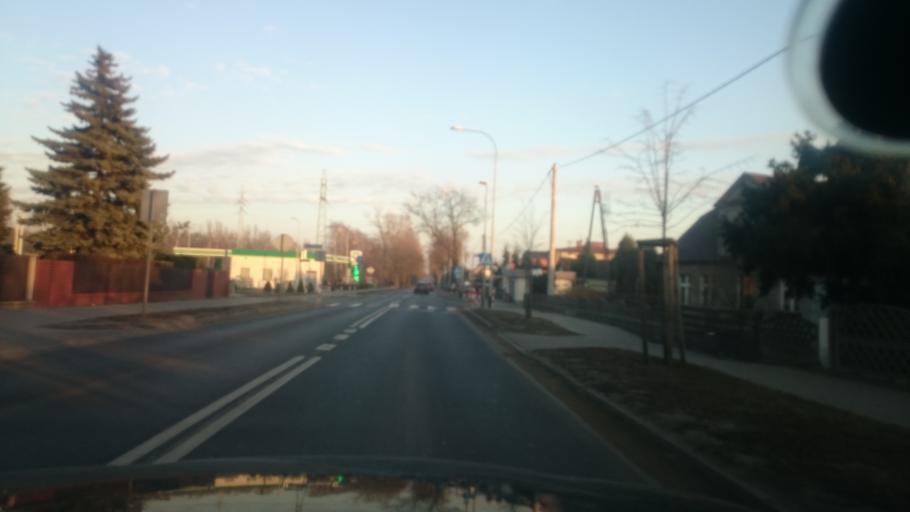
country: PL
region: Greater Poland Voivodeship
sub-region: Powiat ostrowski
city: Ostrow Wielkopolski
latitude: 51.6477
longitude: 17.8496
